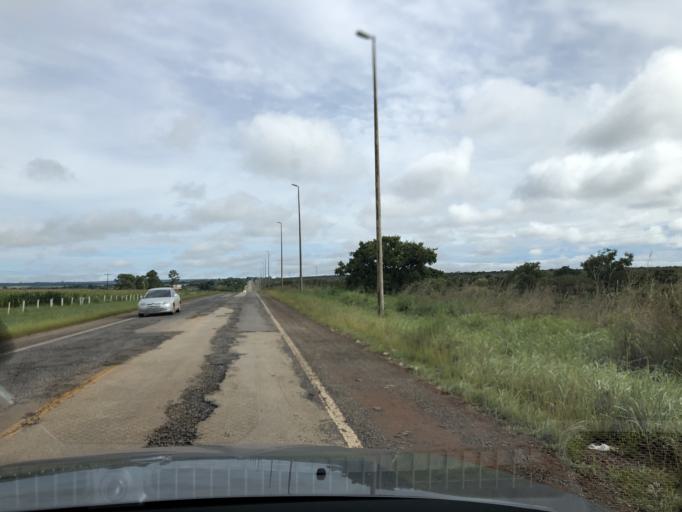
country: BR
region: Federal District
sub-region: Brasilia
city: Brasilia
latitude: -15.7209
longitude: -48.0867
